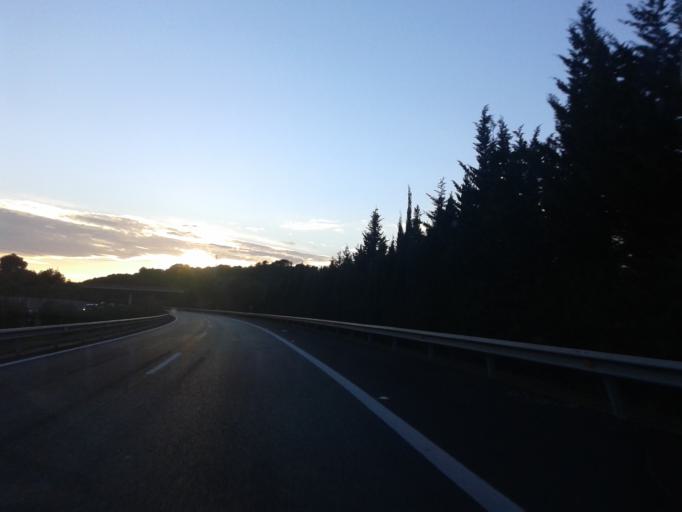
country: ES
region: Catalonia
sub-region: Provincia de Barcelona
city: Cubelles
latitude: 41.2428
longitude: 1.6867
